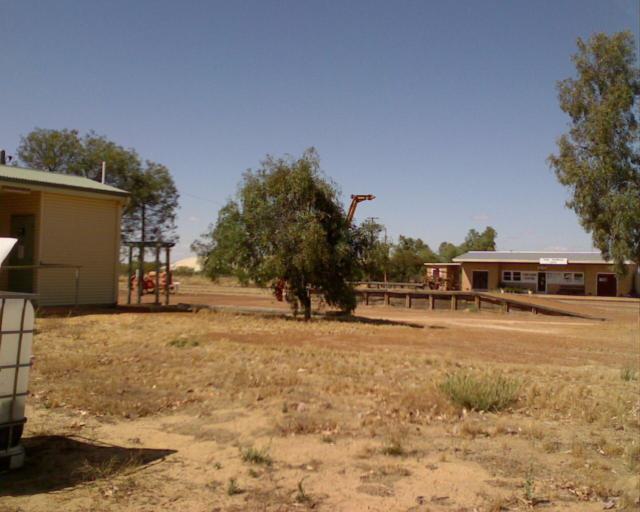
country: AU
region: Western Australia
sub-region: Wongan-Ballidu
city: Wongan Hills
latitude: -30.1068
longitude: 116.6312
